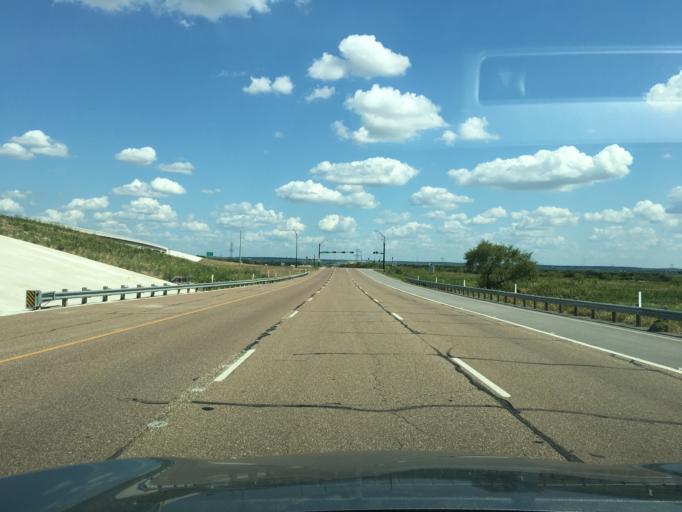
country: US
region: Texas
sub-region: Tarrant County
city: Mansfield
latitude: 32.5231
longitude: -97.0852
